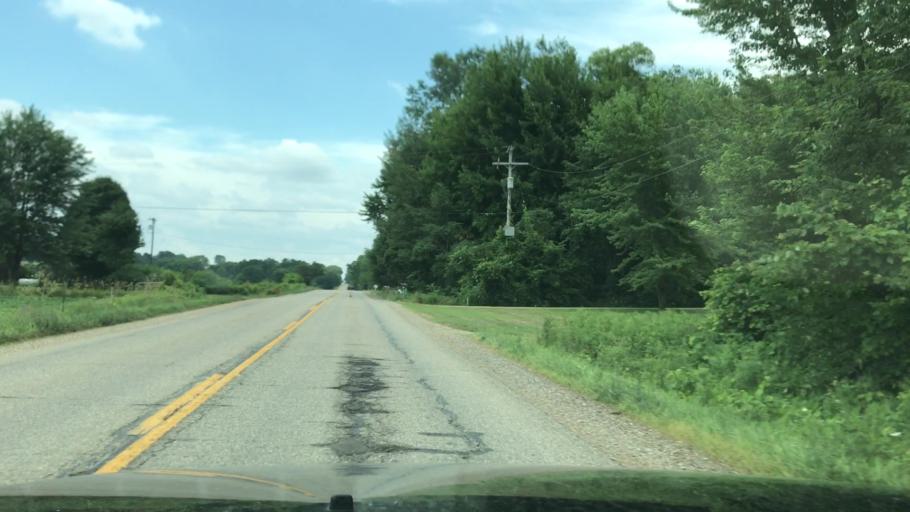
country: US
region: Michigan
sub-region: Ottawa County
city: Hudsonville
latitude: 42.7821
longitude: -85.8841
